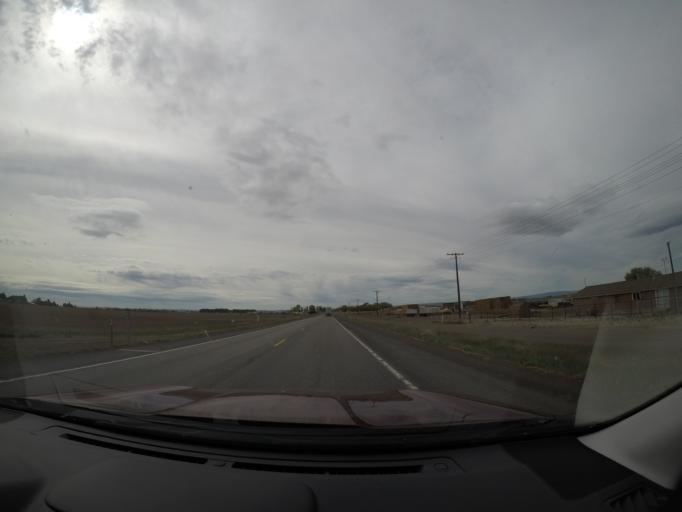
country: US
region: Washington
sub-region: Grant County
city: Quincy
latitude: 47.1099
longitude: -119.8535
